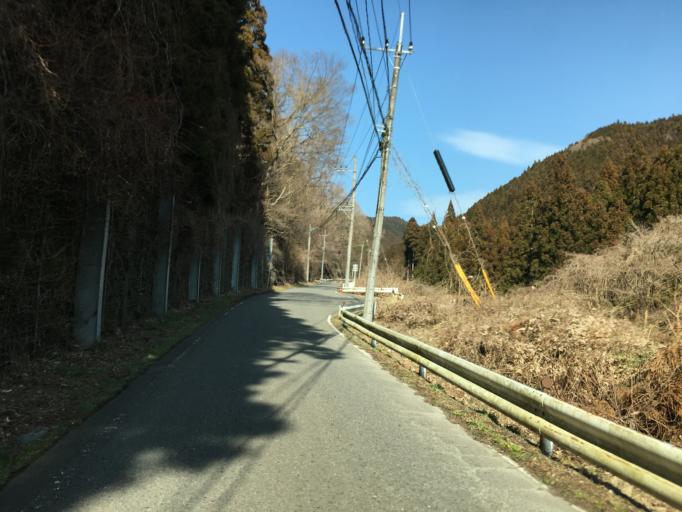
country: JP
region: Ibaraki
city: Daigo
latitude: 36.8036
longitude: 140.4962
